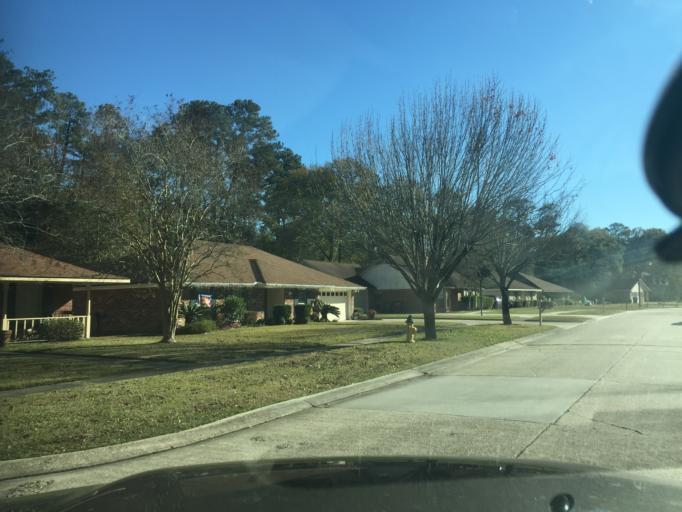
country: US
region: Louisiana
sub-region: Saint Tammany Parish
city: Slidell
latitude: 30.3043
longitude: -89.7455
